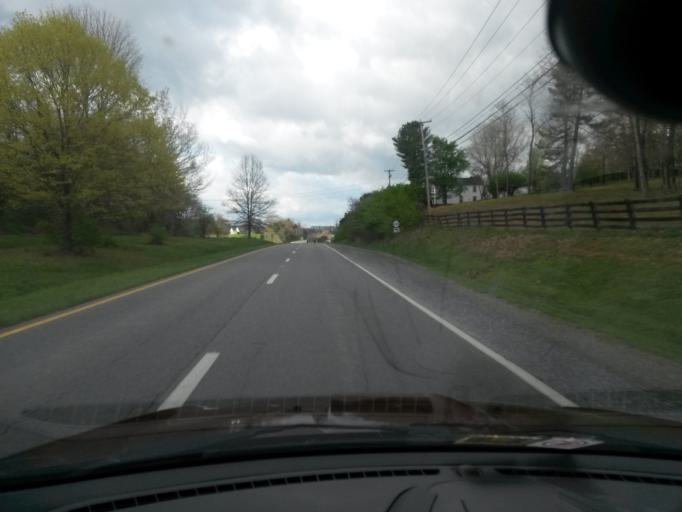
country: US
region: Virginia
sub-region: Botetourt County
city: Fincastle
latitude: 37.4786
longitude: -79.8796
